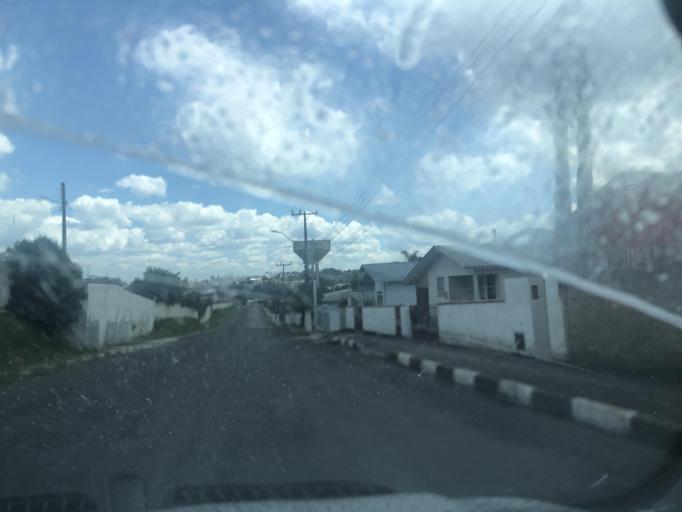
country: BR
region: Santa Catarina
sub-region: Lages
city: Lages
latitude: -27.7904
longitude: -50.3114
